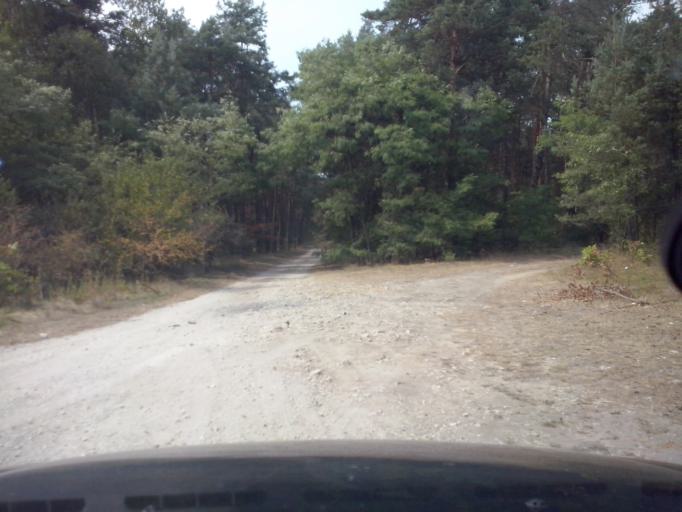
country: PL
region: Swietokrzyskie
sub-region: Powiat kielecki
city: Brzeziny
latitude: 50.7599
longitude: 20.5449
